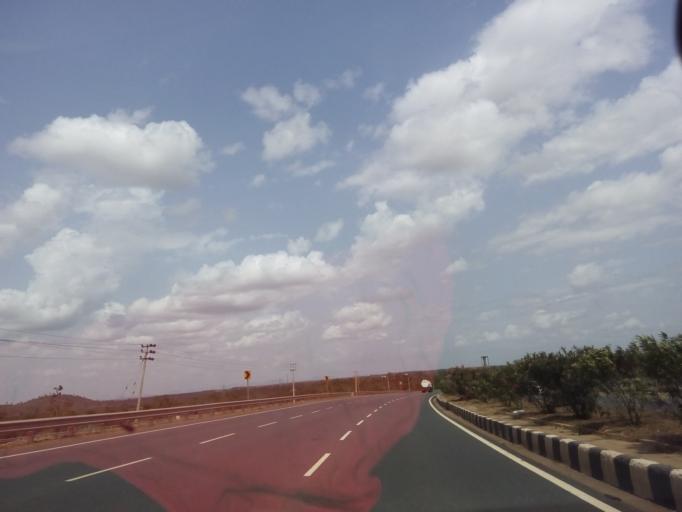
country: IN
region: Karnataka
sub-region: Chitradurga
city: Hiriyur
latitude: 13.8505
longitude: 76.7239
